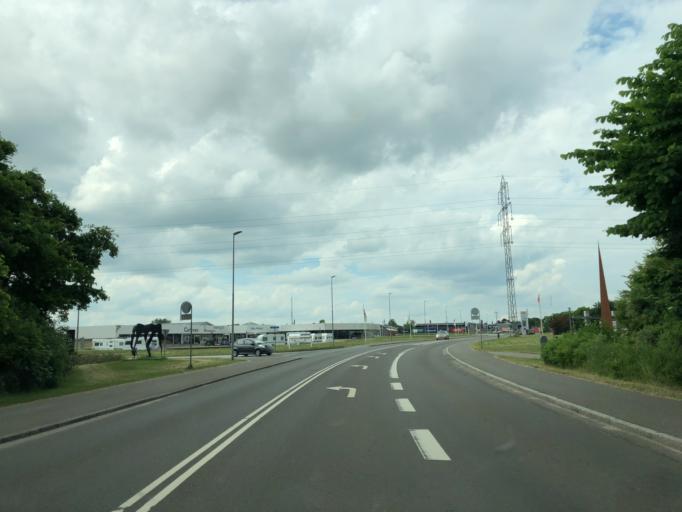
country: DK
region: Central Jutland
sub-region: Struer Kommune
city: Struer
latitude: 56.4807
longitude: 8.5877
